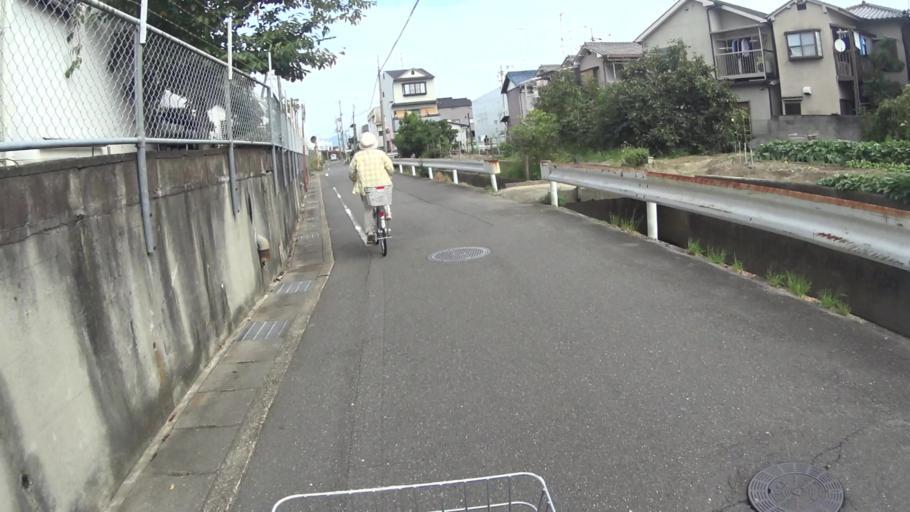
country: JP
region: Kyoto
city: Muko
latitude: 34.9437
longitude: 135.7108
